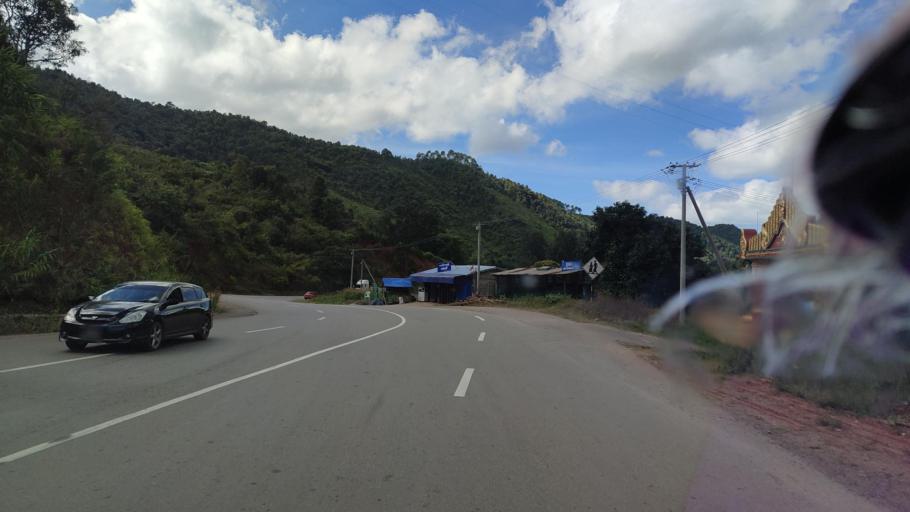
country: MM
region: Mandalay
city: Yamethin
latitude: 20.6598
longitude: 96.5413
